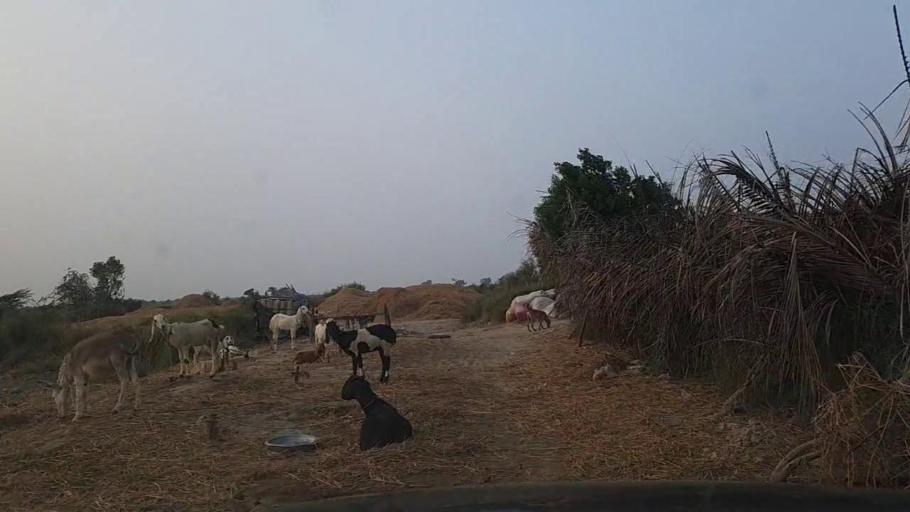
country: PK
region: Sindh
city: Gharo
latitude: 24.7387
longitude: 67.7062
